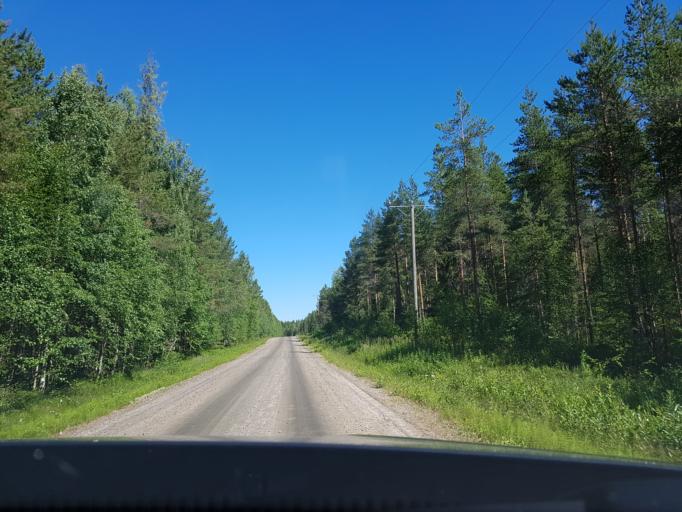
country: FI
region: Kainuu
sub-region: Kehys-Kainuu
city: Kuhmo
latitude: 64.1891
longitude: 29.5999
